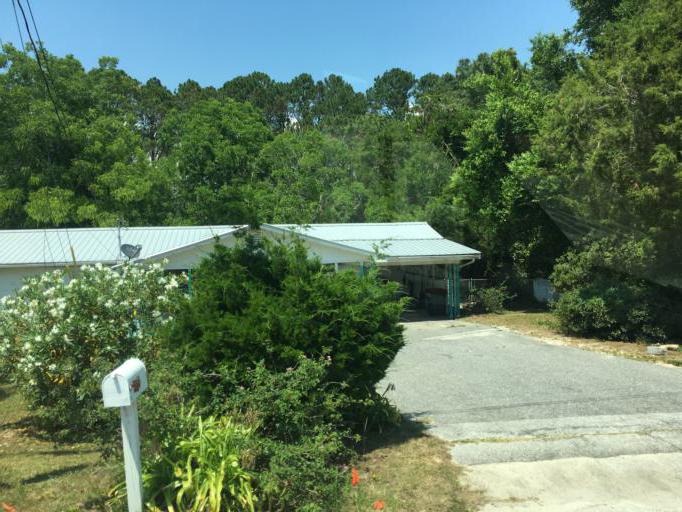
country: US
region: Florida
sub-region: Bay County
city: Laguna Beach
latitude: 30.2318
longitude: -85.8829
